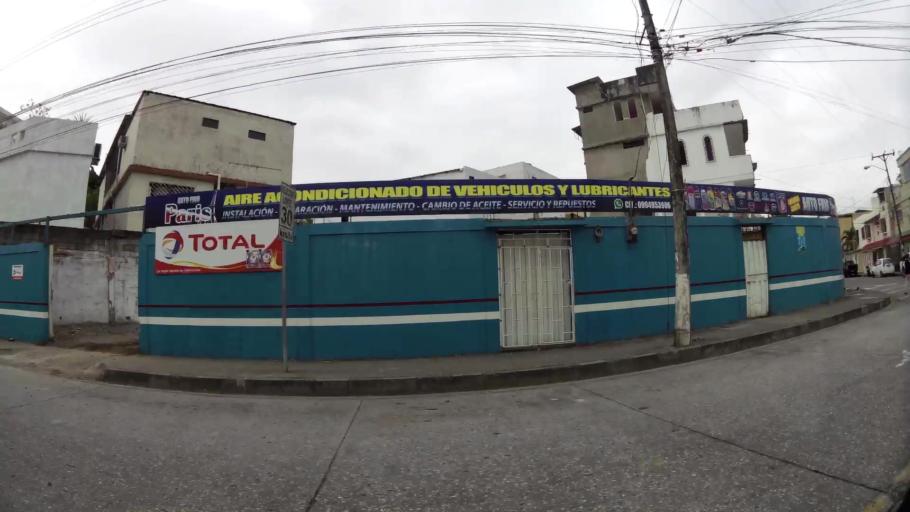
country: EC
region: Guayas
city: Eloy Alfaro
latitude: -2.1531
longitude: -79.8923
